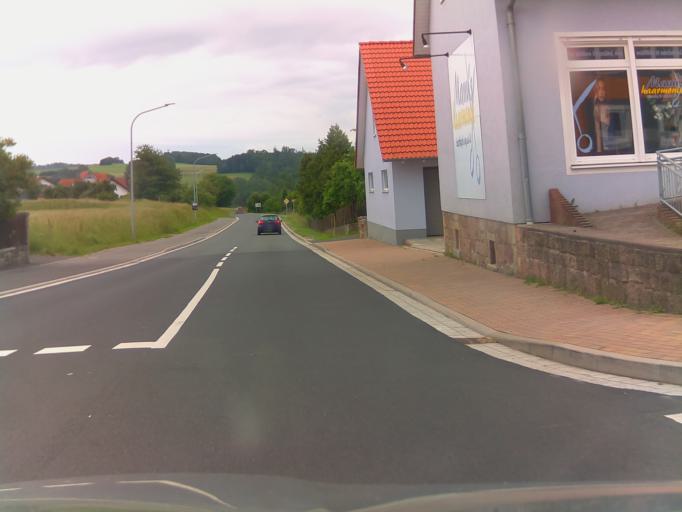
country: DE
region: Bavaria
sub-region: Regierungsbezirk Unterfranken
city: Oberleichtersbach
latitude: 50.2669
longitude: 9.8139
